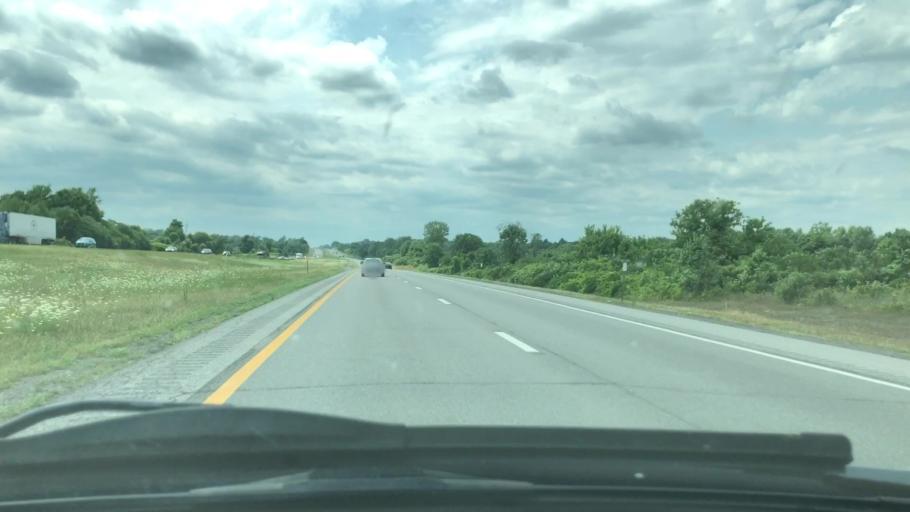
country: US
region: New York
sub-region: Genesee County
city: Oakfield
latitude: 43.0165
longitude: -78.2723
